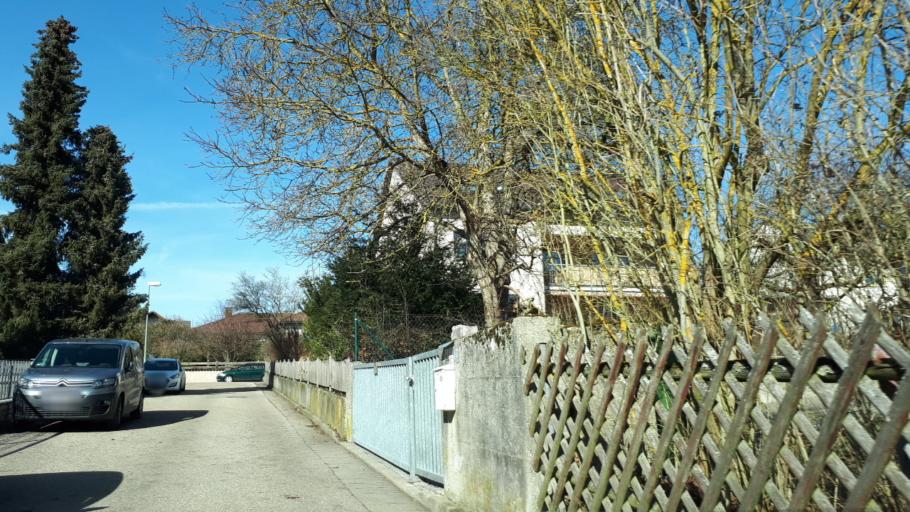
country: DE
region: Bavaria
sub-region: Upper Palatinate
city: Pentling
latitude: 48.9841
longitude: 12.0559
